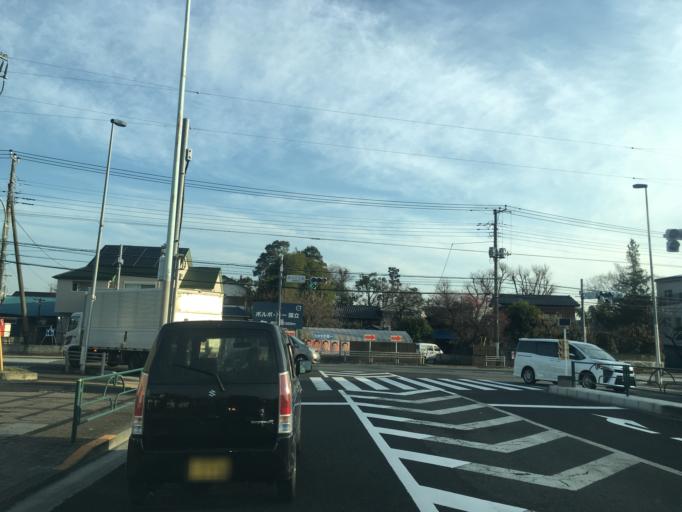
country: JP
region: Tokyo
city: Hino
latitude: 35.6822
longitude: 139.4292
